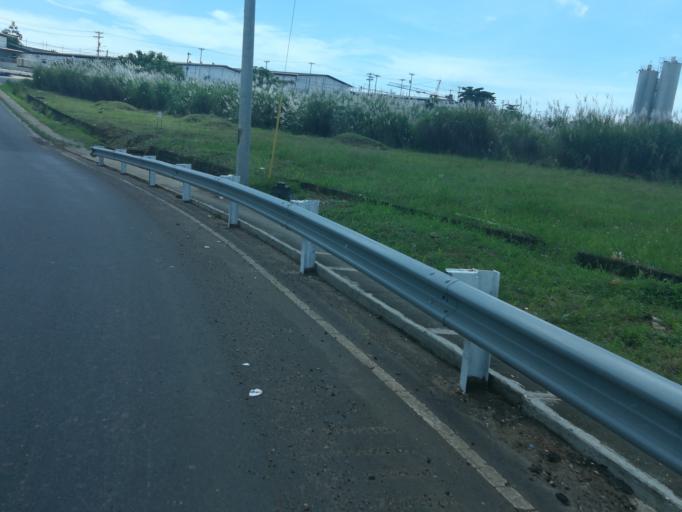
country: PA
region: Panama
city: Tocumen
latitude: 9.0907
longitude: -79.3999
